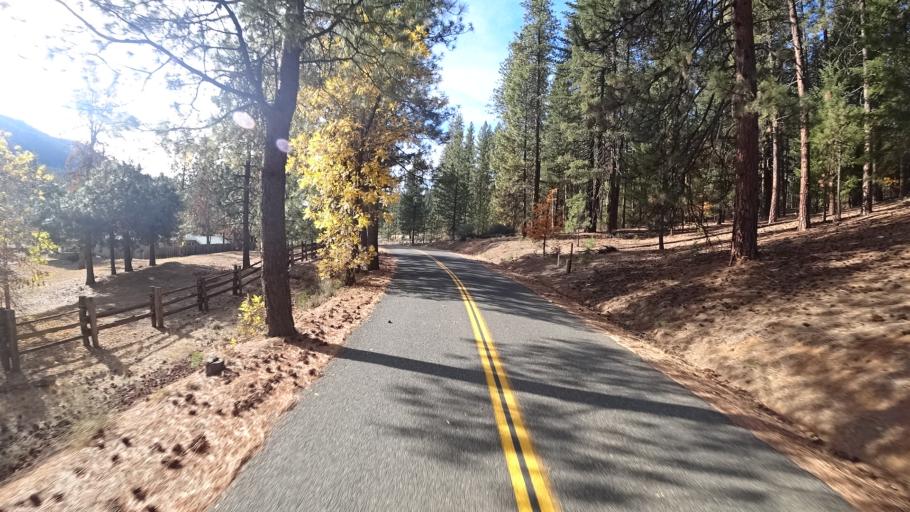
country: US
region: California
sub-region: Siskiyou County
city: Yreka
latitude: 41.6775
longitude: -122.8315
